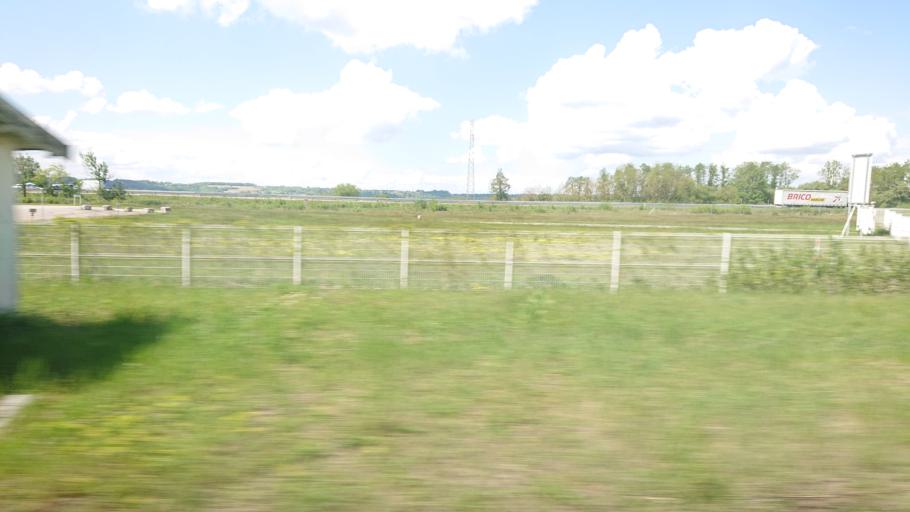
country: FR
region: Rhone-Alpes
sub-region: Departement de l'Ain
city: Leyment
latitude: 45.9368
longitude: 5.2855
